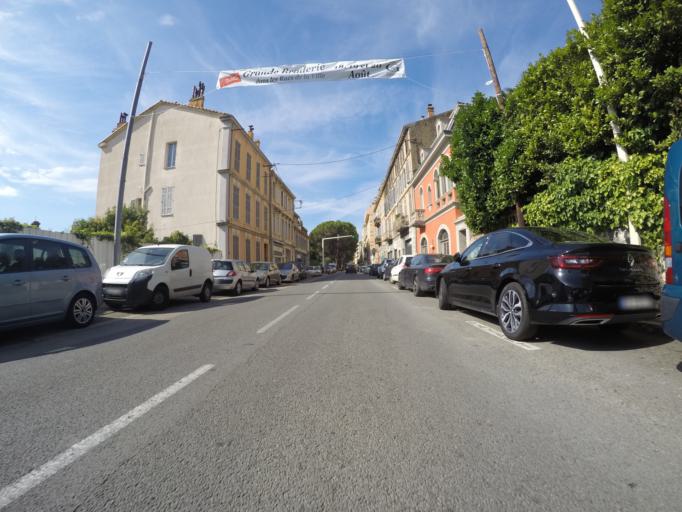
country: FR
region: Provence-Alpes-Cote d'Azur
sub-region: Departement des Alpes-Maritimes
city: Grasse
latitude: 43.6636
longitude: 6.9250
